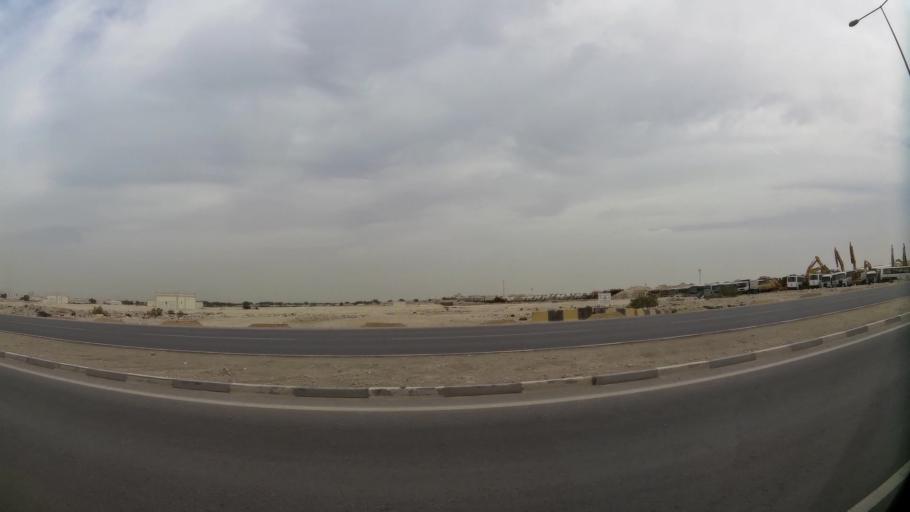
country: QA
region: Baladiyat ad Dawhah
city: Doha
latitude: 25.2324
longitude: 51.4710
